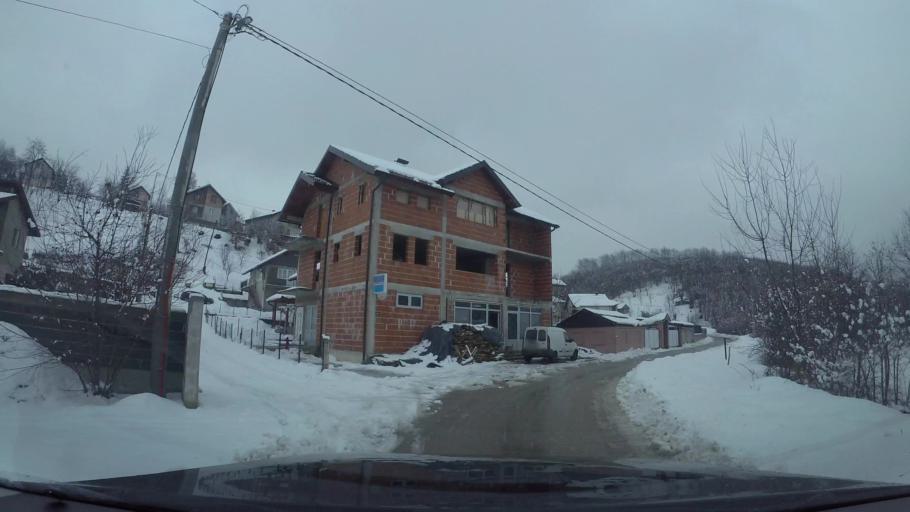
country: BA
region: Federation of Bosnia and Herzegovina
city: Hadzici
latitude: 43.8483
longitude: 18.2536
